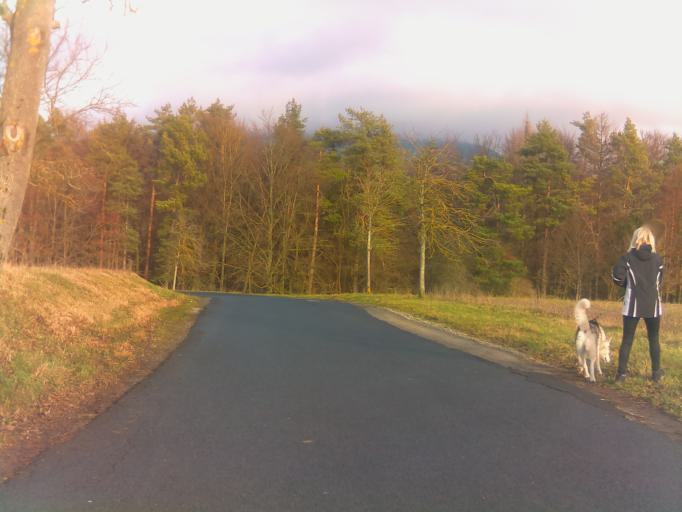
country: DE
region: Thuringia
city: Utendorf
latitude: 50.5982
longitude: 10.4383
